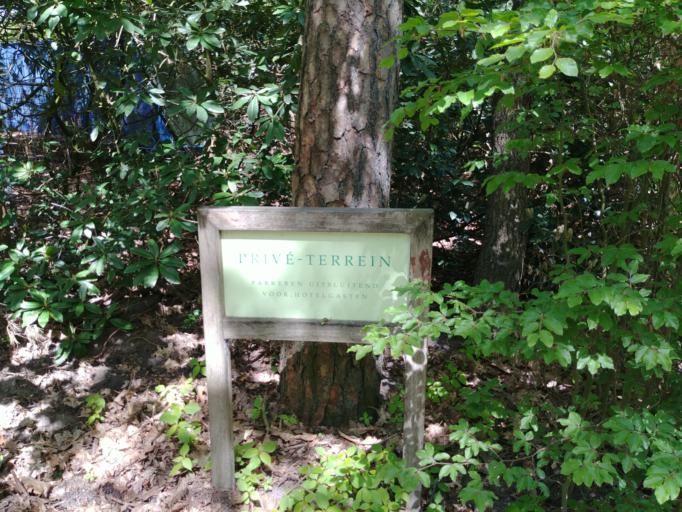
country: NL
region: Gelderland
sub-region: Gemeente Barneveld
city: Garderen
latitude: 52.3061
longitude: 5.7103
